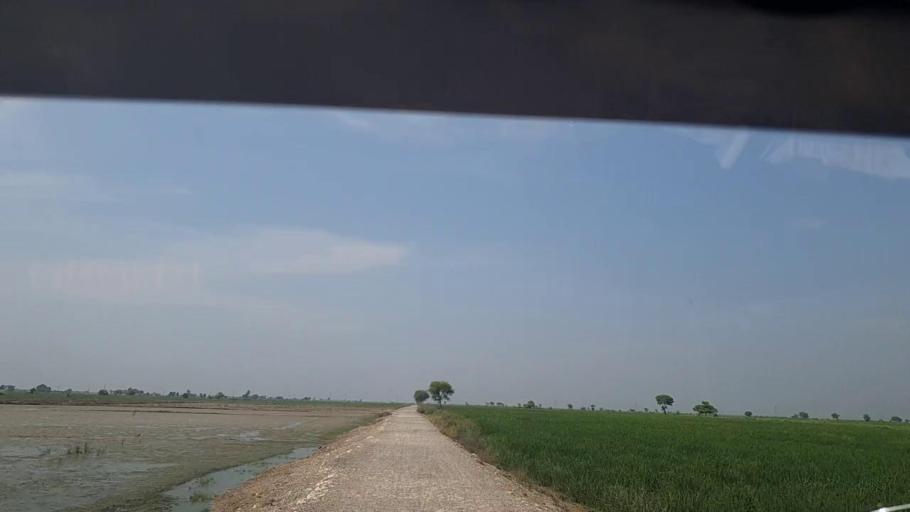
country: PK
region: Sindh
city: Thul
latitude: 28.2105
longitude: 68.6876
